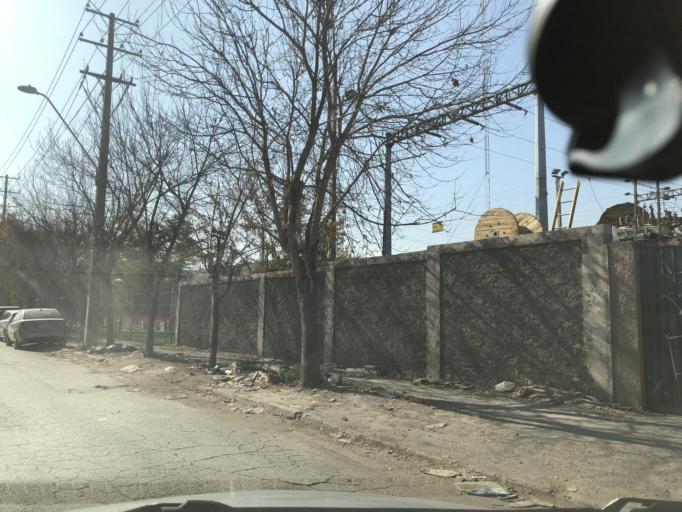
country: CL
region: Santiago Metropolitan
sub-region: Provincia de Cordillera
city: Puente Alto
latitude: -33.6197
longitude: -70.5670
